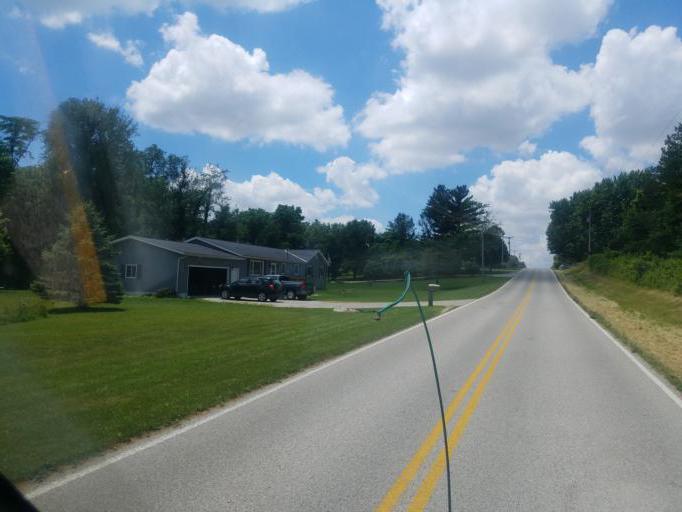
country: US
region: Ohio
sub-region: Huron County
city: Willard
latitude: 41.0794
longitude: -82.7298
